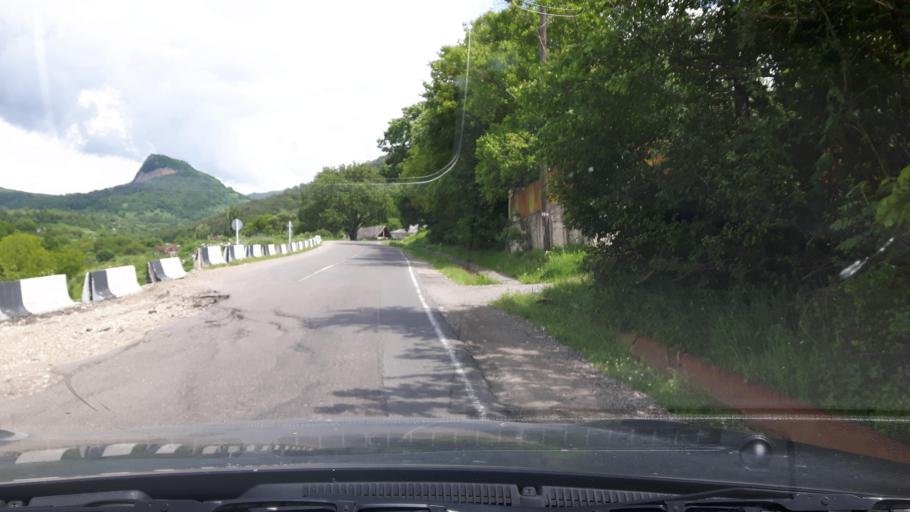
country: GE
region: Kakheti
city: Sagarejo
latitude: 41.8581
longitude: 45.2122
